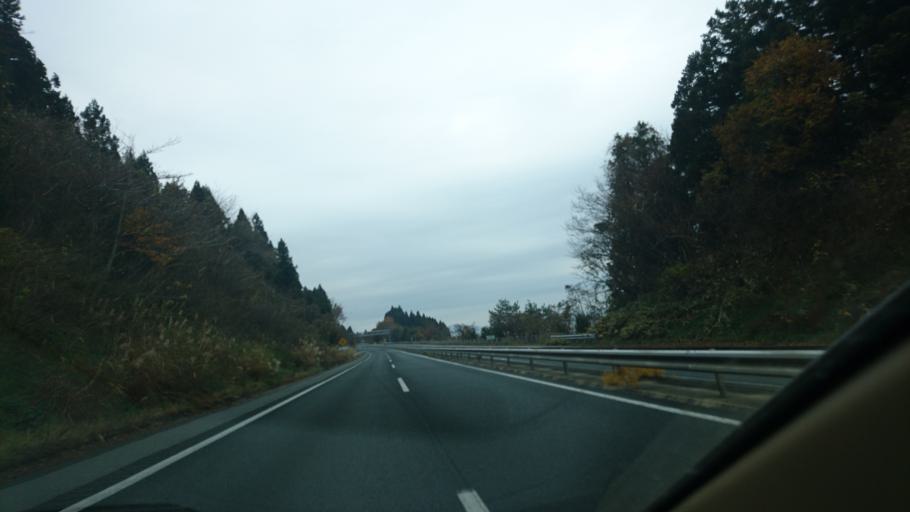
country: JP
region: Iwate
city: Kitakami
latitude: 39.2767
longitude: 141.0690
